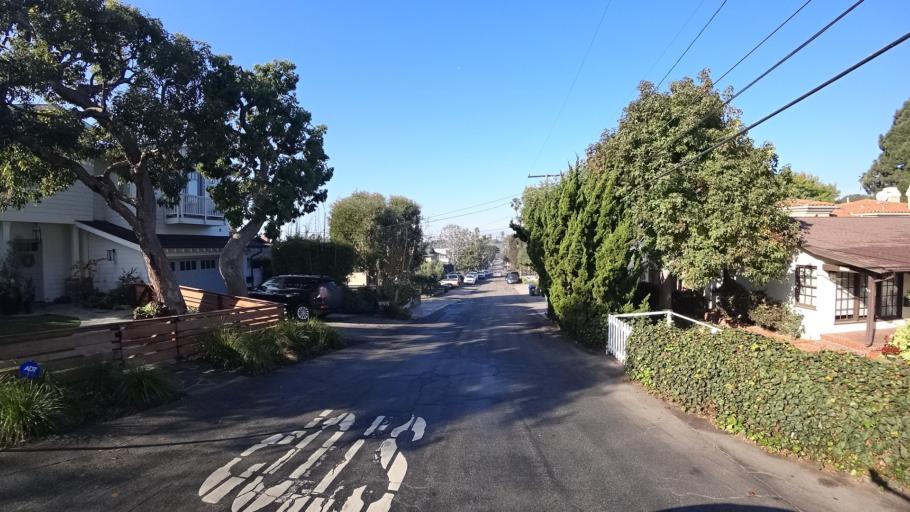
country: US
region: California
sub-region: Los Angeles County
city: Manhattan Beach
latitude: 33.8963
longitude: -118.4060
